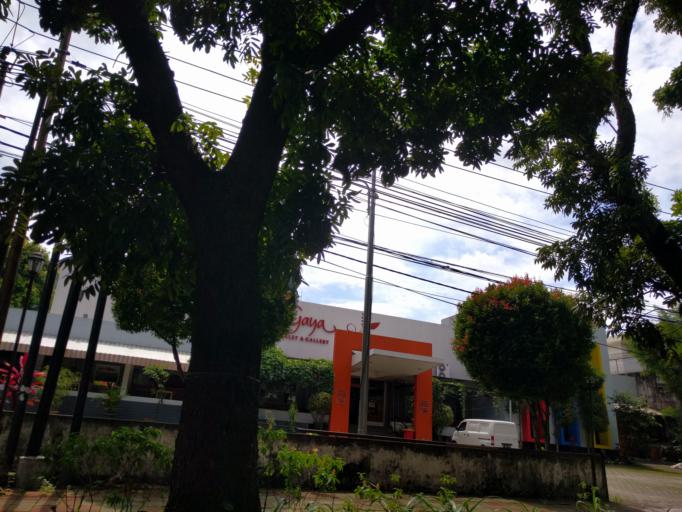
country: ID
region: West Java
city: Bogor
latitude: -6.6117
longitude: 106.8126
